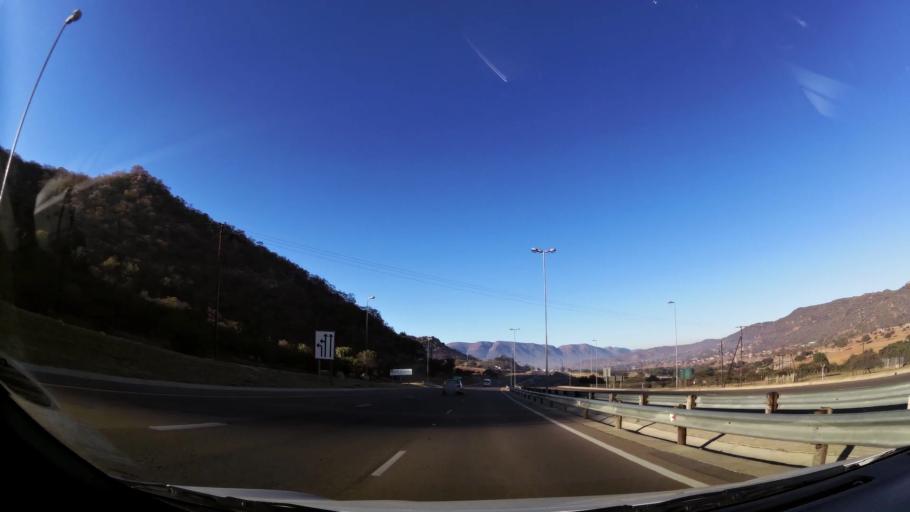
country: ZA
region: Limpopo
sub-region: Capricorn District Municipality
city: Mankoeng
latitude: -23.9246
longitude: 29.7951
